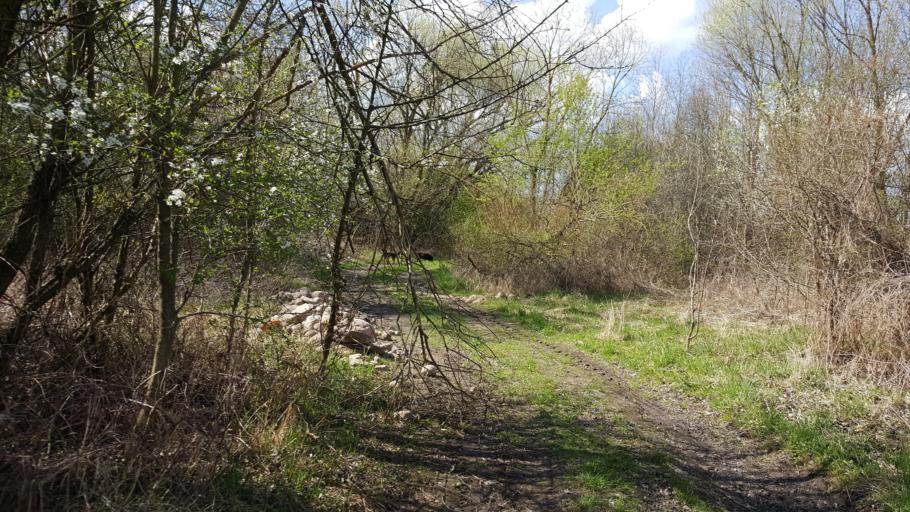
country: BY
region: Brest
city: Kamyanyets
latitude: 52.3876
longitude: 23.6508
